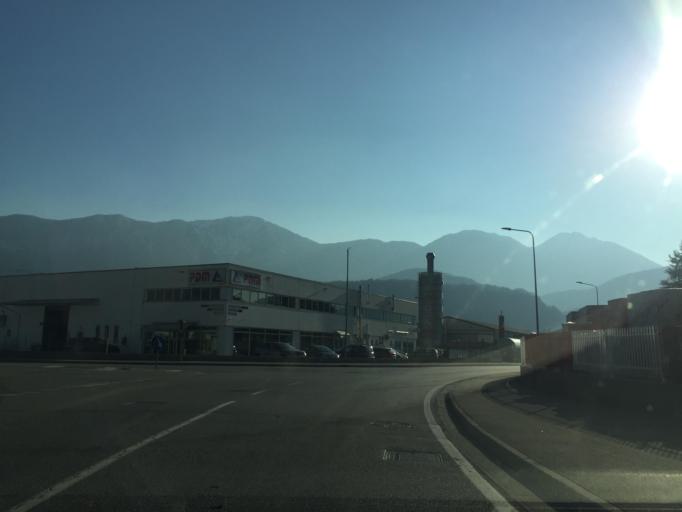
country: IT
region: Friuli Venezia Giulia
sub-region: Provincia di Udine
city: Tolmezzo
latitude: 46.3917
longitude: 13.0314
